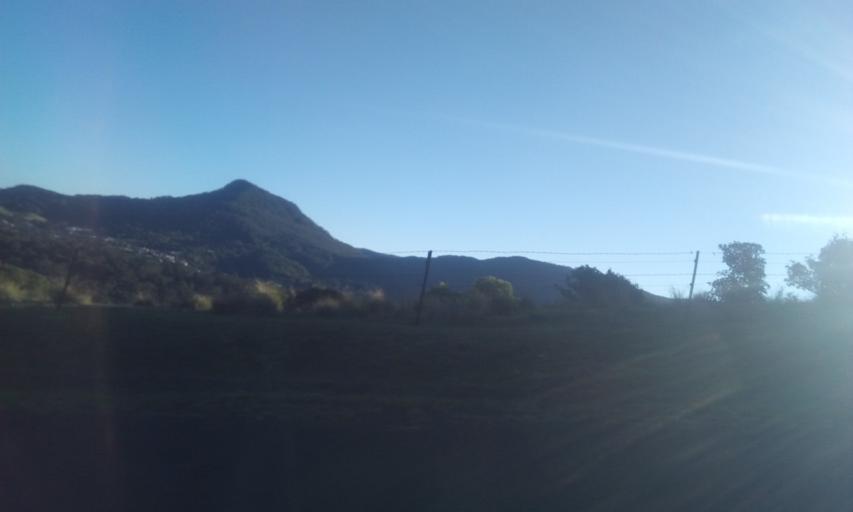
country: AU
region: New South Wales
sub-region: Wollongong
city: Mount Keira
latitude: -34.4253
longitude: 150.8421
